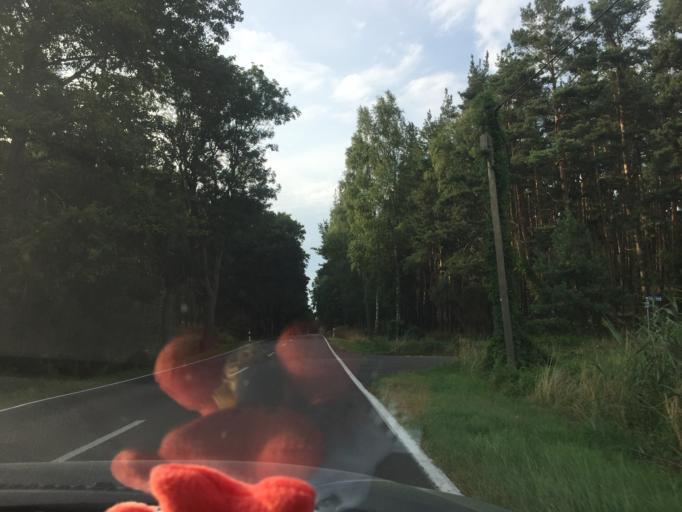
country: DE
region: Brandenburg
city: Liebenwalde
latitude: 52.9065
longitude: 13.3896
